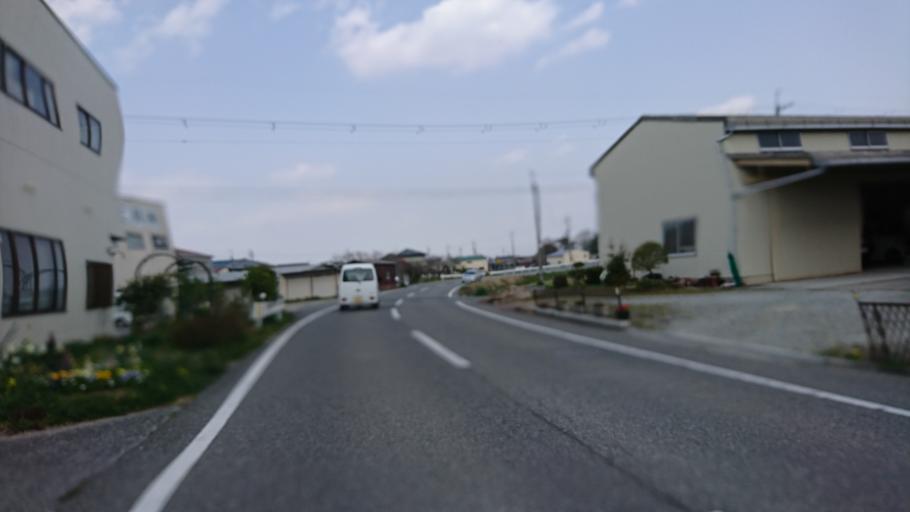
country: JP
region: Hyogo
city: Ono
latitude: 34.8602
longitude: 134.9124
